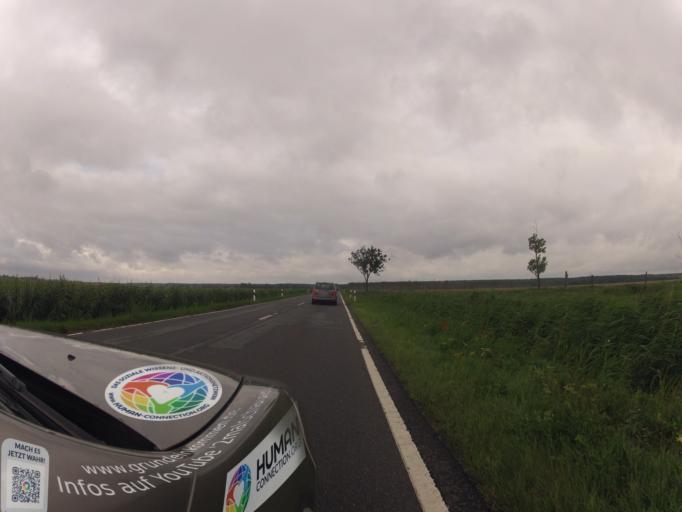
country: DE
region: Mecklenburg-Vorpommern
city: Lassan
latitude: 53.8686
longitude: 13.8163
